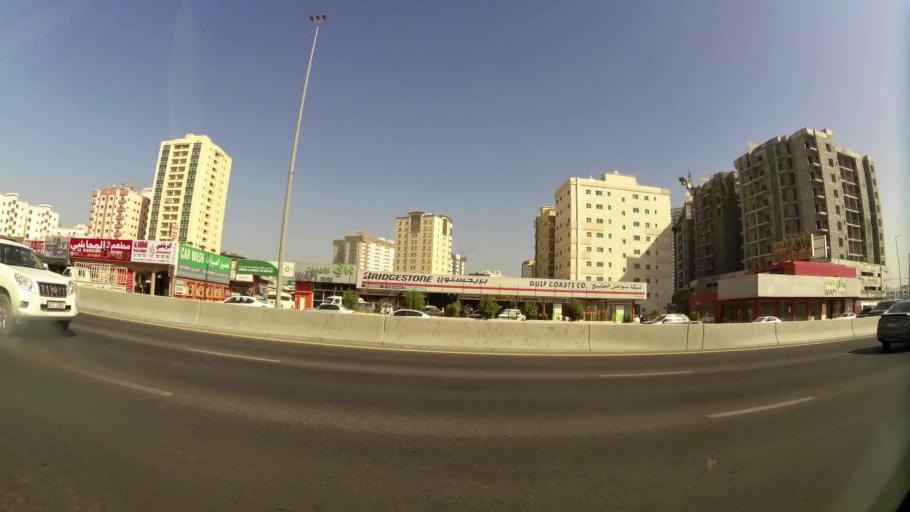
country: AE
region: Ajman
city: Ajman
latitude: 25.3882
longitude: 55.4691
